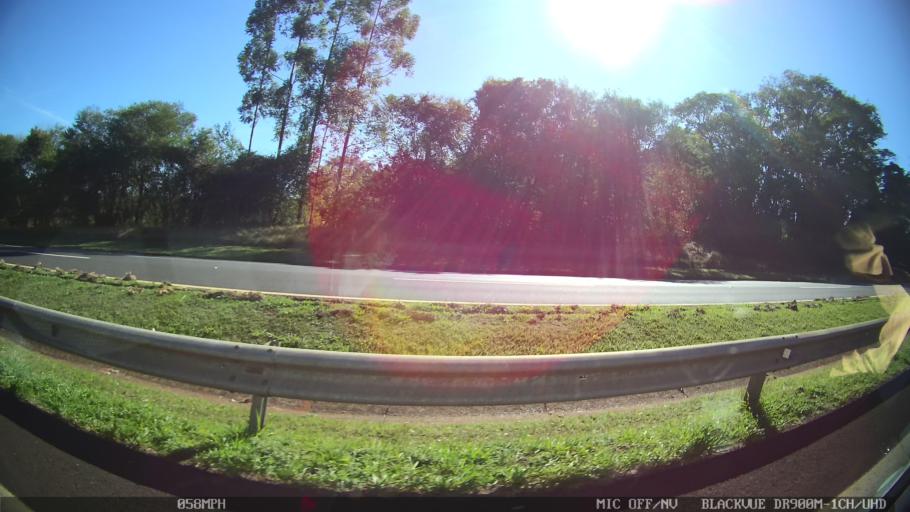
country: BR
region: Sao Paulo
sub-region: Franca
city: Franca
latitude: -20.5770
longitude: -47.3509
